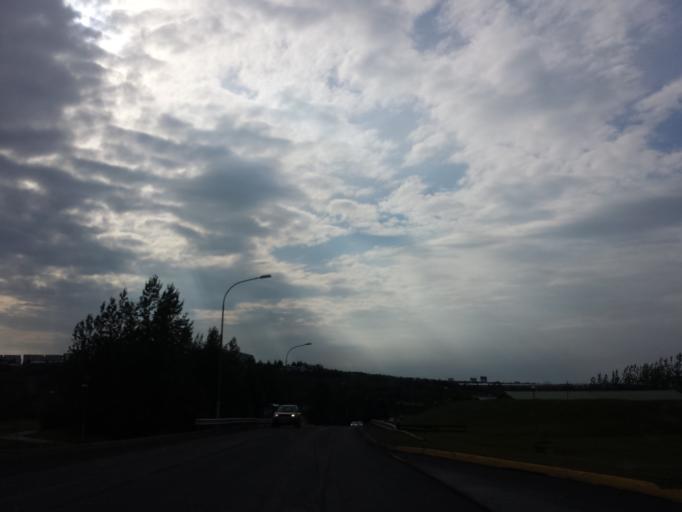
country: IS
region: Capital Region
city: Reykjavik
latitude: 64.1193
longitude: -21.8133
